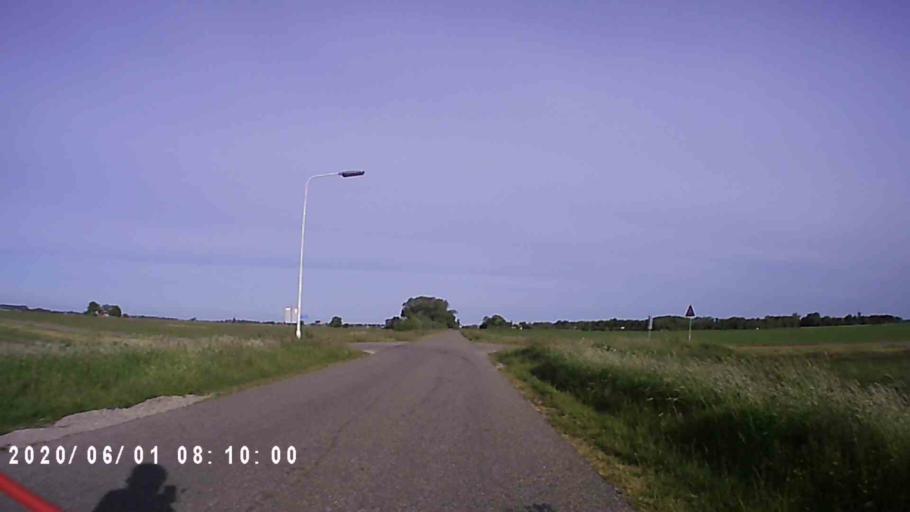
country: NL
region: Friesland
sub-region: Gemeente Ferwerderadiel
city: Burdaard
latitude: 53.2859
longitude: 5.8903
